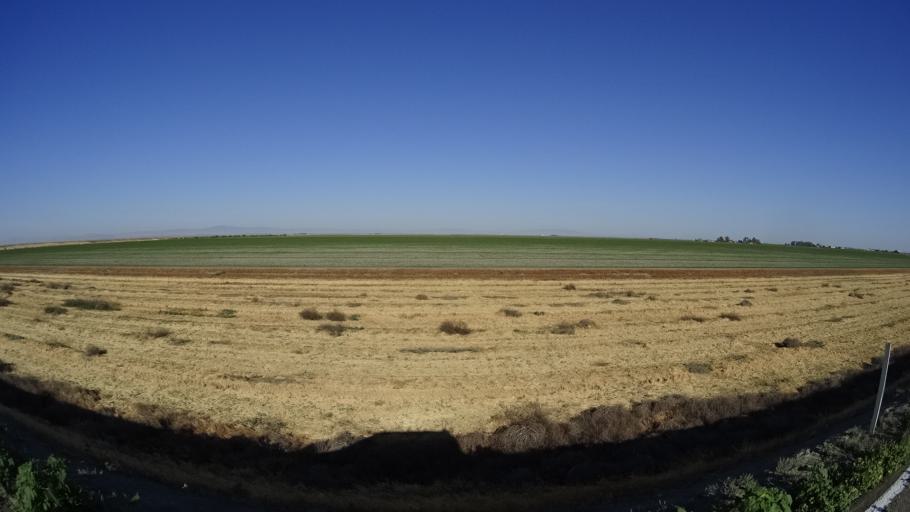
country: US
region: California
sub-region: Kings County
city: Stratford
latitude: 36.1432
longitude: -119.7981
